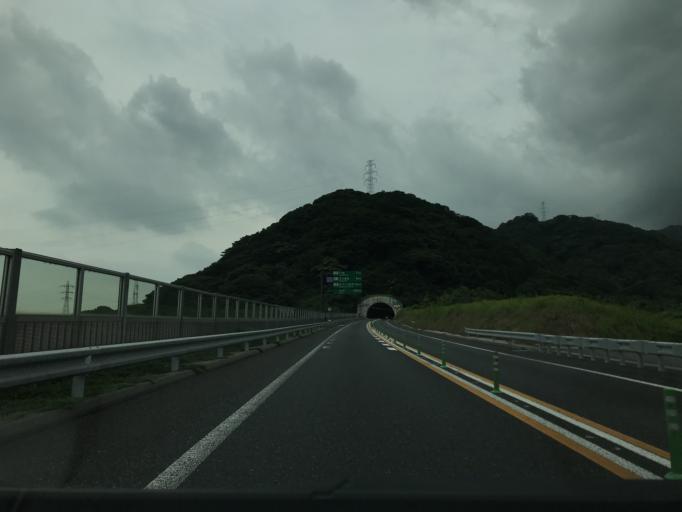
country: JP
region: Fukuoka
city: Kanda
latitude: 33.7794
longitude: 130.9711
